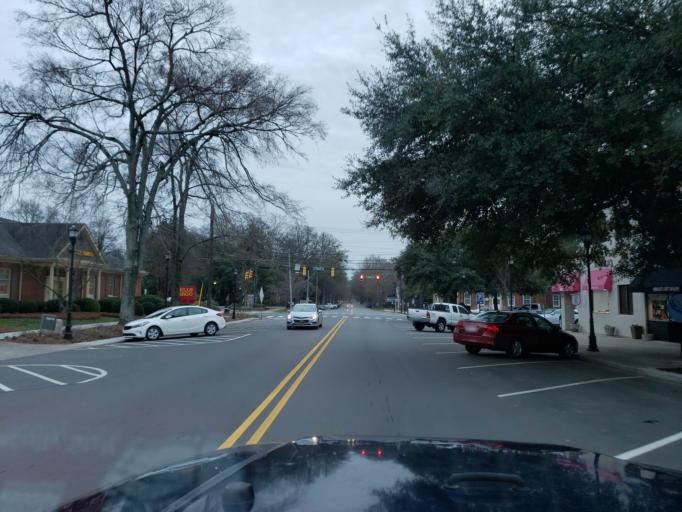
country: US
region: North Carolina
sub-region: Cleveland County
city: Shelby
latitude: 35.2900
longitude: -81.5391
